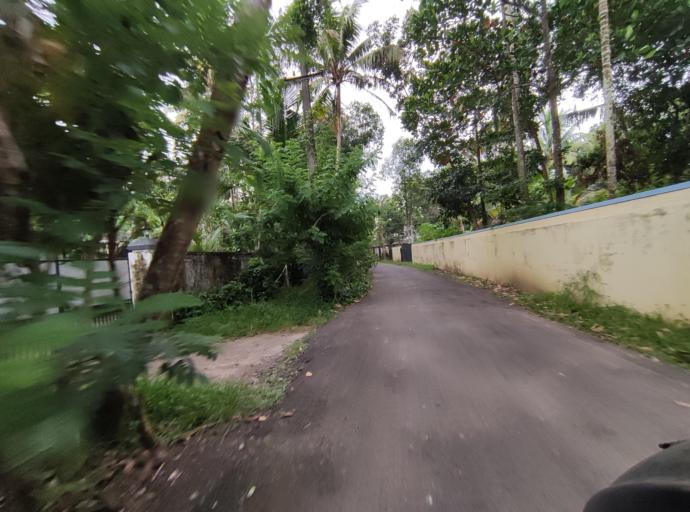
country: IN
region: Kerala
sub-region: Alappuzha
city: Shertallai
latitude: 9.6667
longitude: 76.3480
